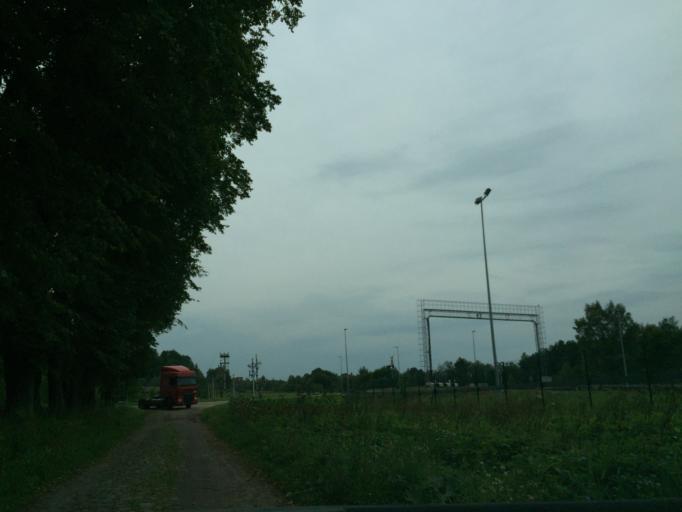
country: LV
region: Zilupes
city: Zilupe
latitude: 56.3920
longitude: 28.1096
